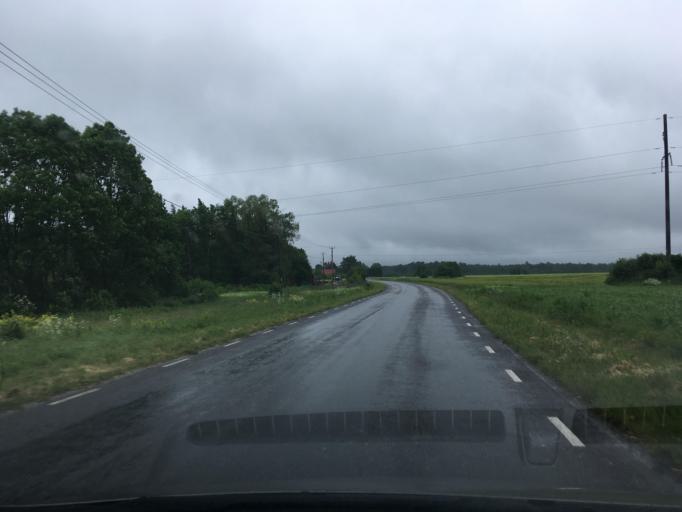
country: EE
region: Laeaene
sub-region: Lihula vald
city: Lihula
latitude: 58.6625
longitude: 23.7709
